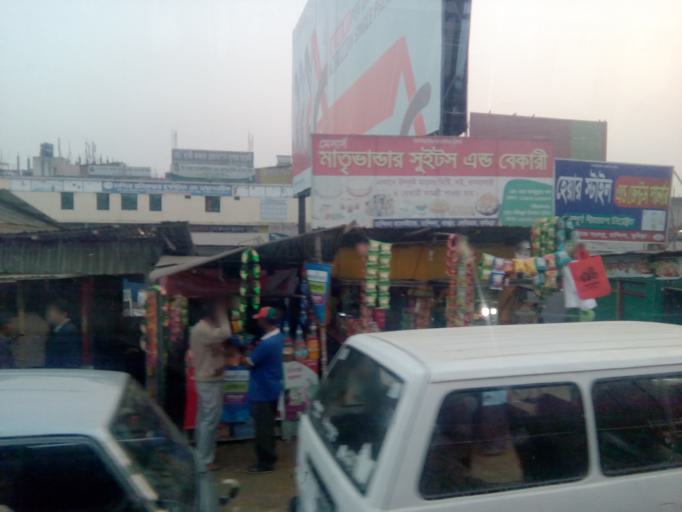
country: BD
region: Chittagong
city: Comilla
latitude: 23.4895
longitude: 91.0046
